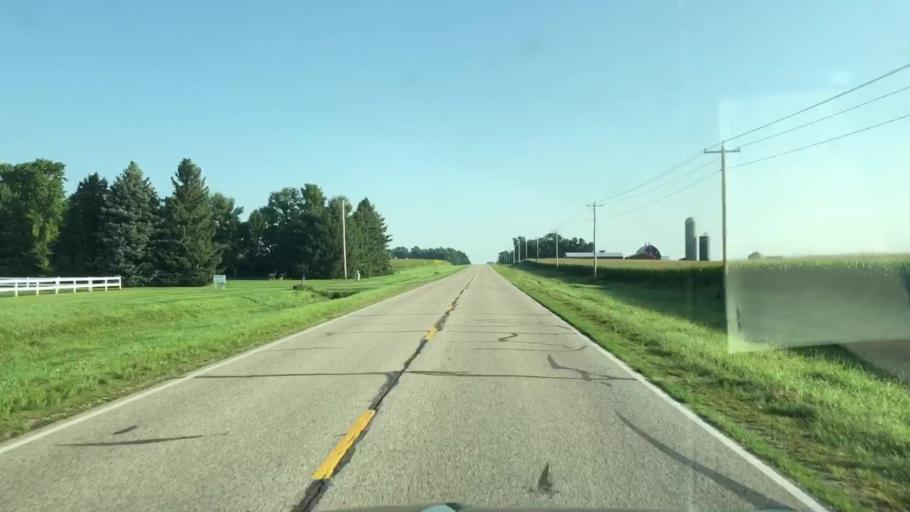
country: US
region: Iowa
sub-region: Lyon County
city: George
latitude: 43.3685
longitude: -95.9983
